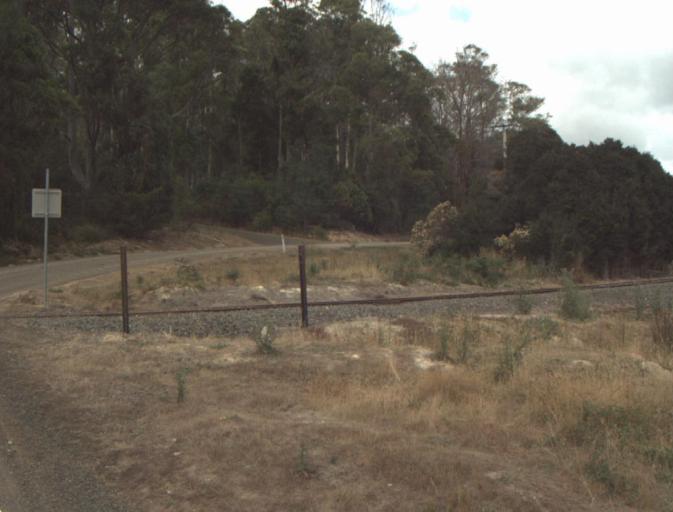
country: AU
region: Tasmania
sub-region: Dorset
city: Bridport
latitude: -41.1759
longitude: 147.2655
